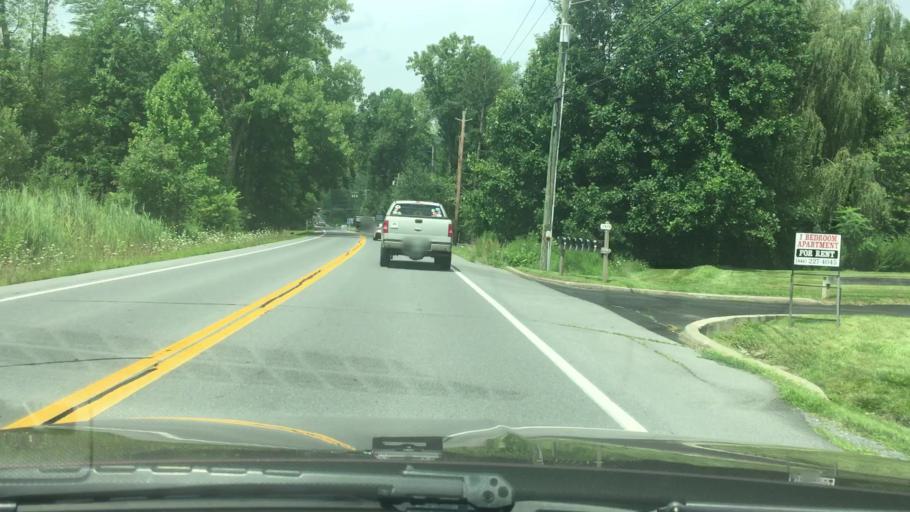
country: US
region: New York
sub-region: Dutchess County
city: Hillside Lake
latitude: 41.6278
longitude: -73.6928
